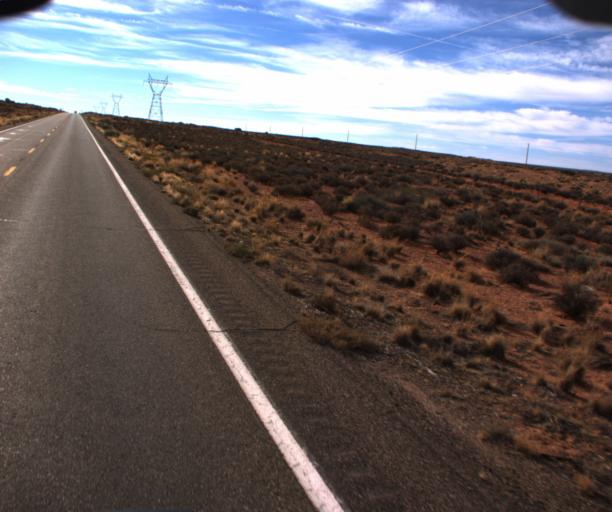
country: US
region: Arizona
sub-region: Coconino County
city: LeChee
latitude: 36.8552
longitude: -111.3363
